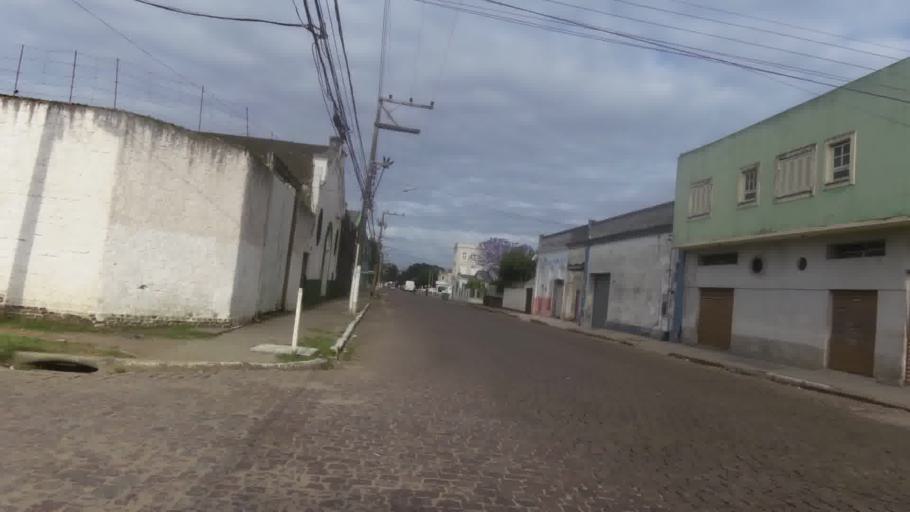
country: BR
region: Rio Grande do Sul
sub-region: Rio Grande
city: Rio Grande
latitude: -32.0314
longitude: -52.0854
